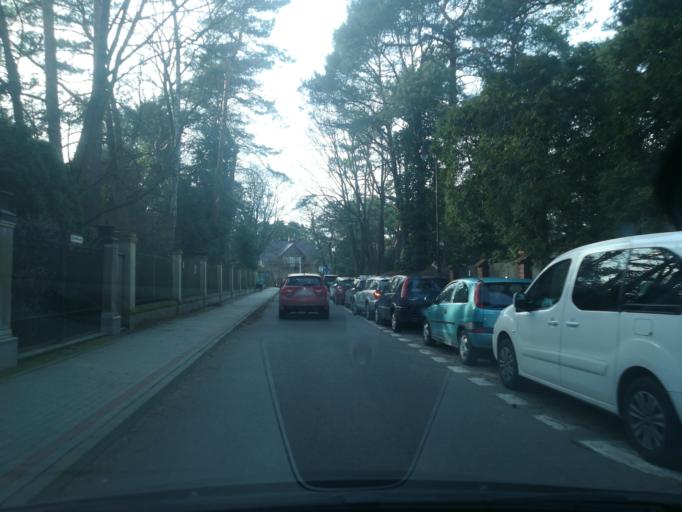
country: PL
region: Masovian Voivodeship
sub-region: Powiat piaseczynski
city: Konstancin-Jeziorna
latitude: 52.0830
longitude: 21.1180
